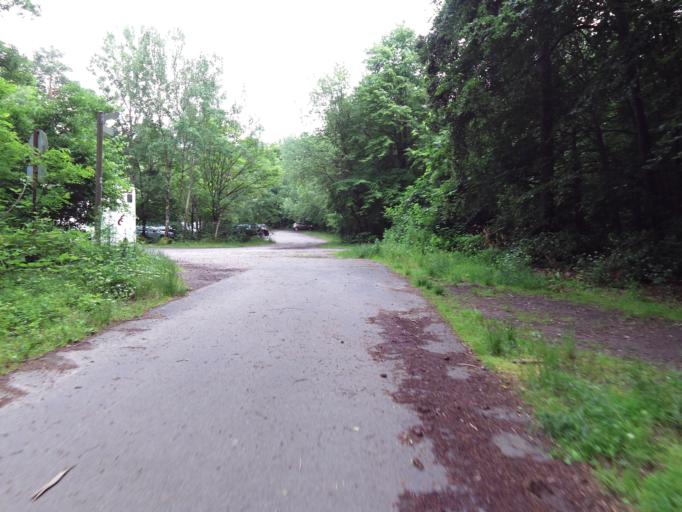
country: DE
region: Rheinland-Pfalz
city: Weisenheim am Berg
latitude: 49.4804
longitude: 8.1191
